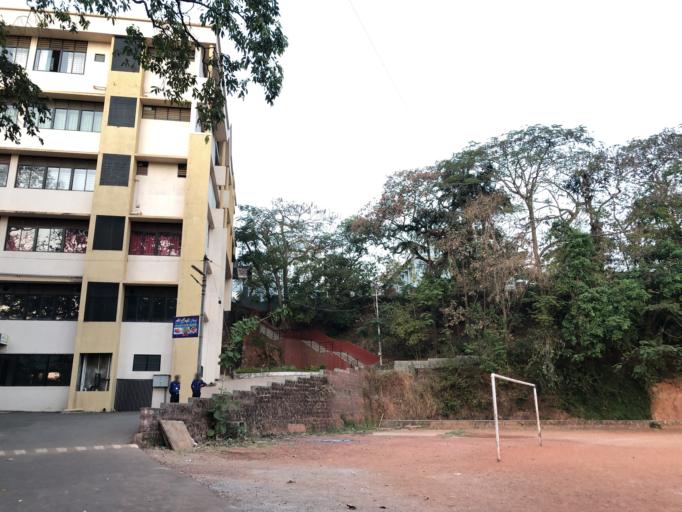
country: IN
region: Karnataka
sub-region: Dakshina Kannada
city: Mangalore
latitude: 12.8734
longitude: 74.8445
